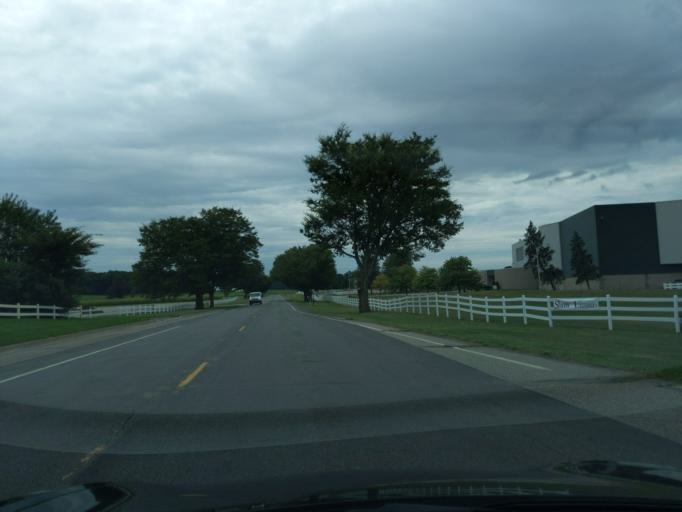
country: US
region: Michigan
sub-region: Ingham County
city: East Lansing
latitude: 42.7088
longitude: -84.4783
